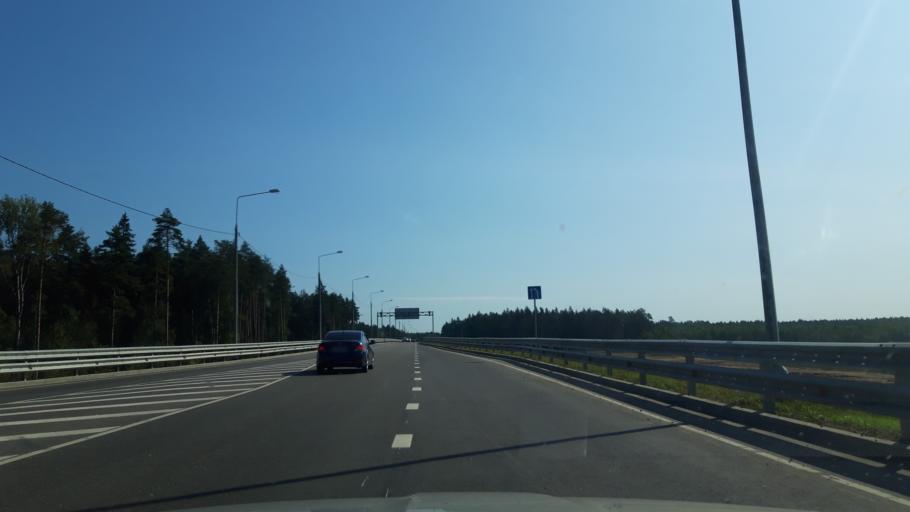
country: RU
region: Tverskaya
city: Novozavidovskiy
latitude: 56.5743
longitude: 36.4690
